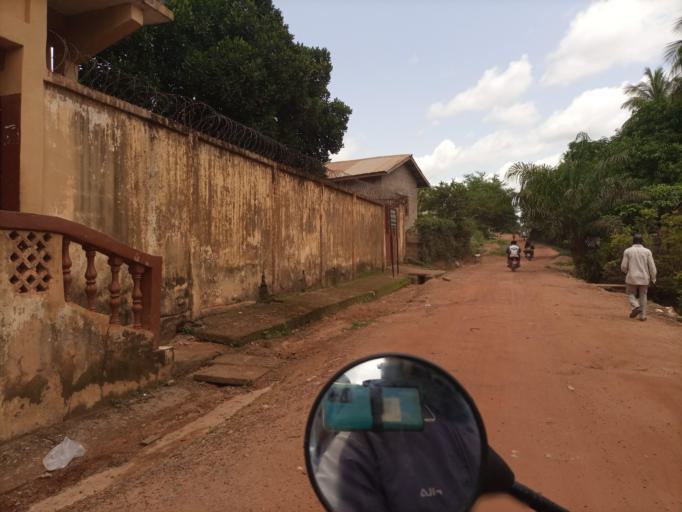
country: SL
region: Southern Province
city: Bo
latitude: 7.9526
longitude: -11.7357
